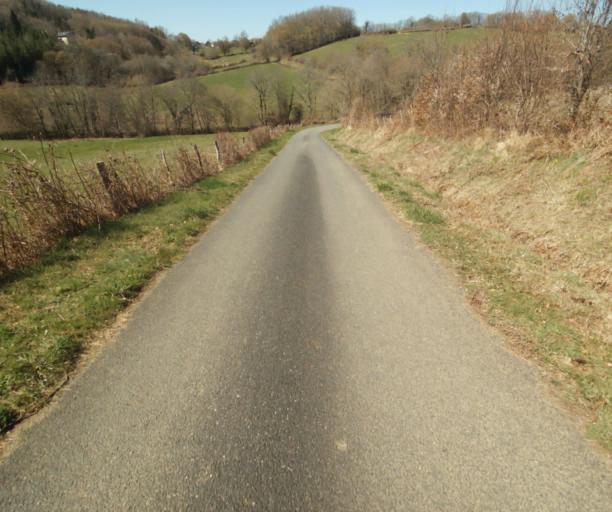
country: FR
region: Limousin
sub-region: Departement de la Correze
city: Chamboulive
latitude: 45.4575
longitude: 1.6780
